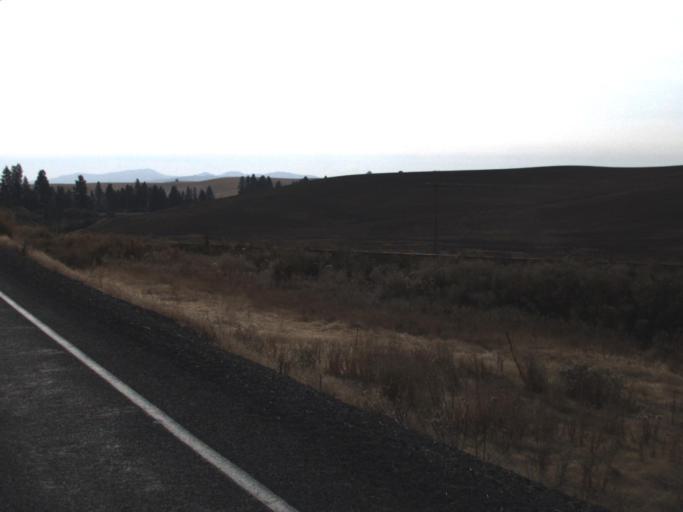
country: US
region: Washington
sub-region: Whitman County
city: Pullman
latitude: 46.9686
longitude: -117.1165
